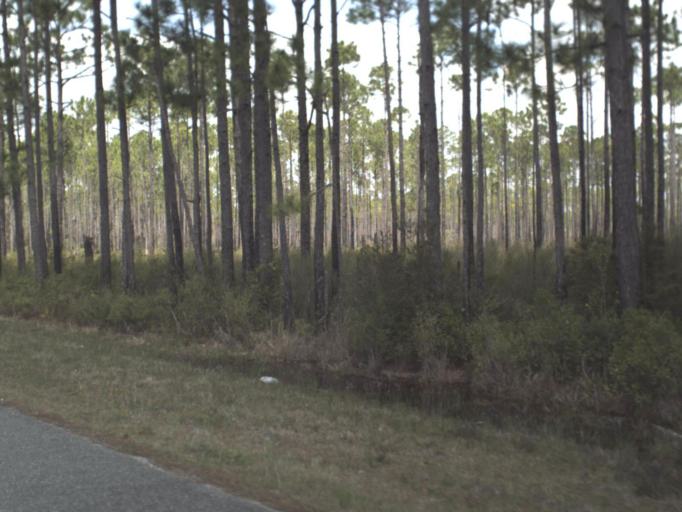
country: US
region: Florida
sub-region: Franklin County
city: Eastpoint
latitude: 29.8135
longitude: -84.8443
